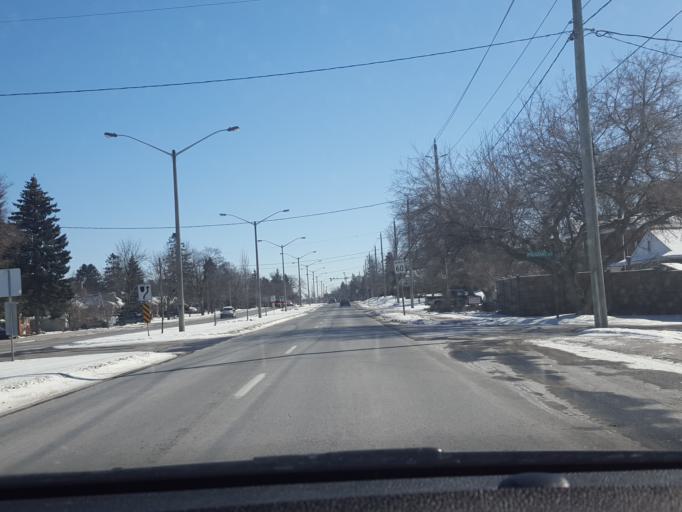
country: CA
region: Ontario
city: Cambridge
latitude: 43.3864
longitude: -80.3403
